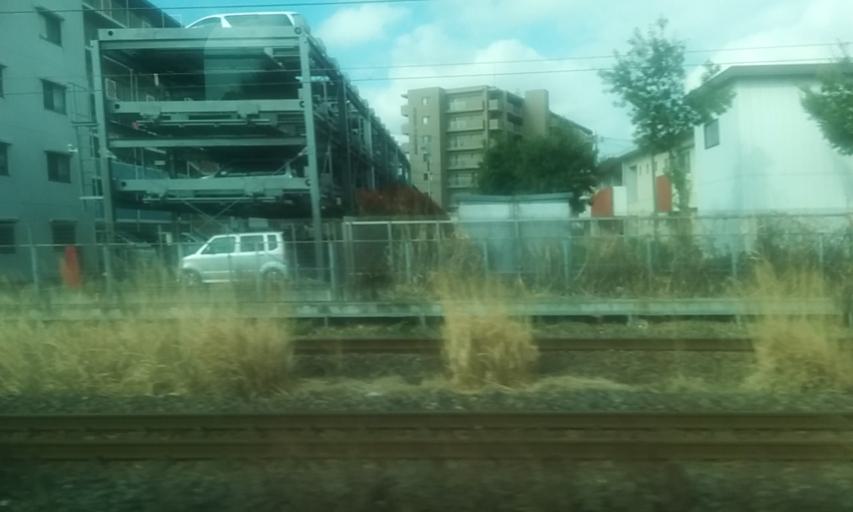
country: JP
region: Kanagawa
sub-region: Kawasaki-shi
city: Kawasaki
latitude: 35.5307
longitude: 139.6785
